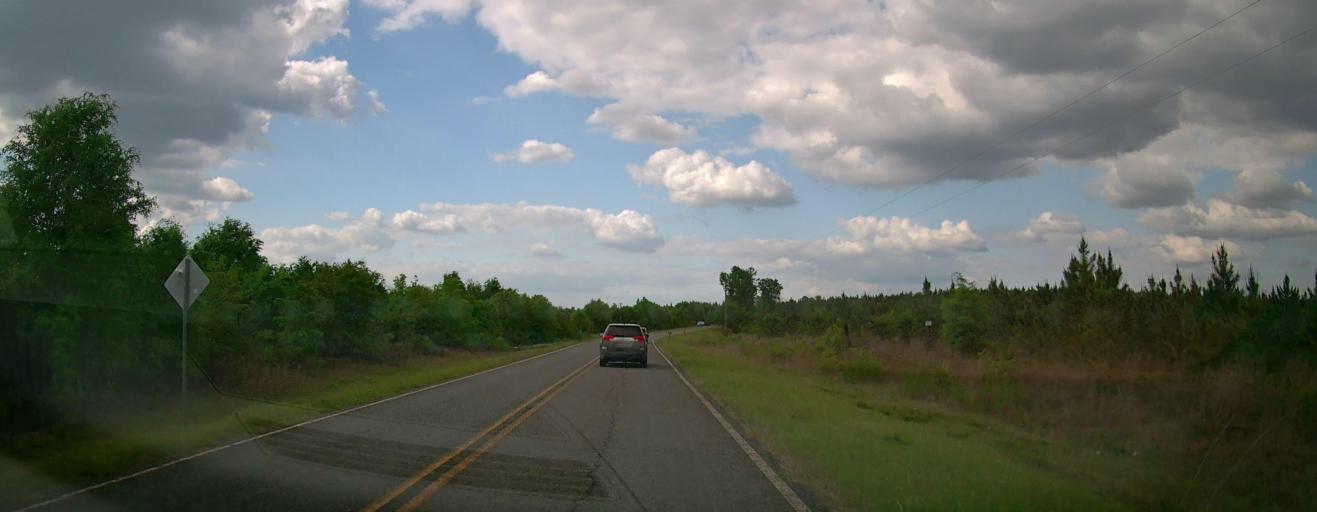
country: US
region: Georgia
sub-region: Washington County
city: Tennille
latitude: 32.7620
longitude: -82.9302
